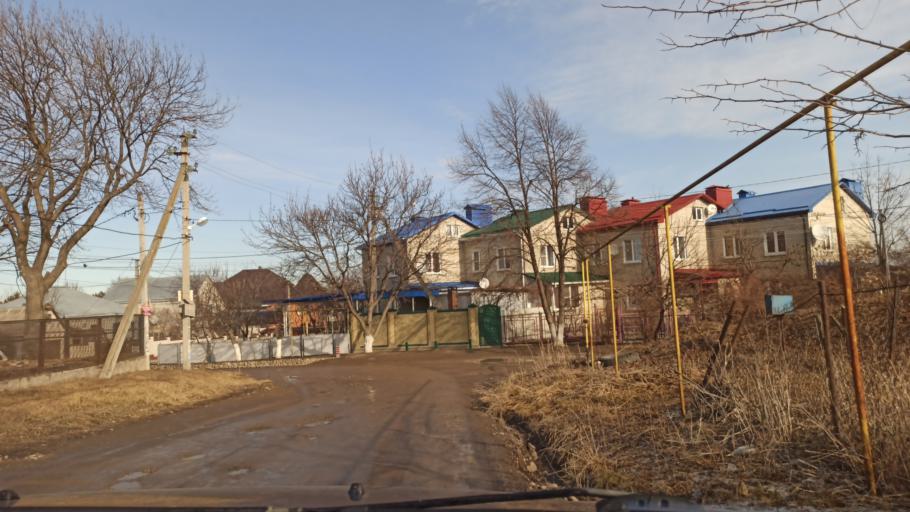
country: RU
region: Stavropol'skiy
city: Yessentukskaya
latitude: 44.0208
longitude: 42.8723
